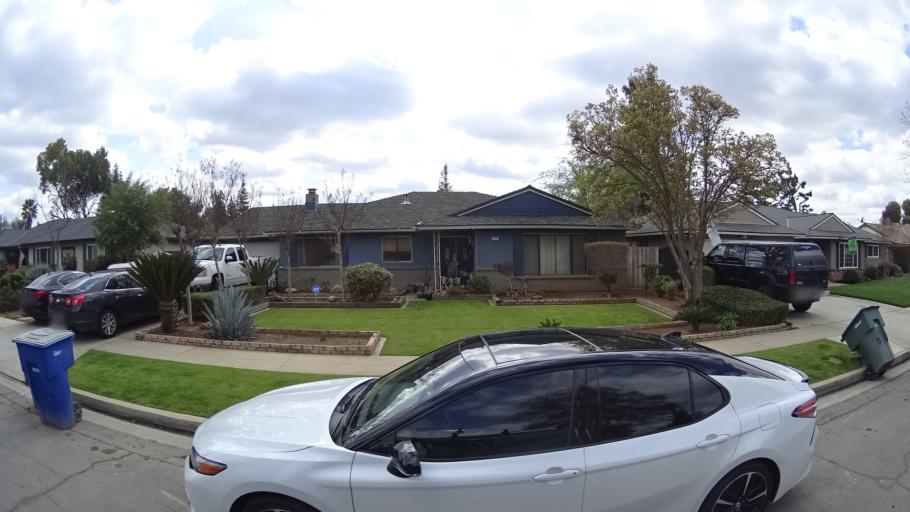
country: US
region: California
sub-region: Fresno County
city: Fresno
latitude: 36.8348
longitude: -119.8160
